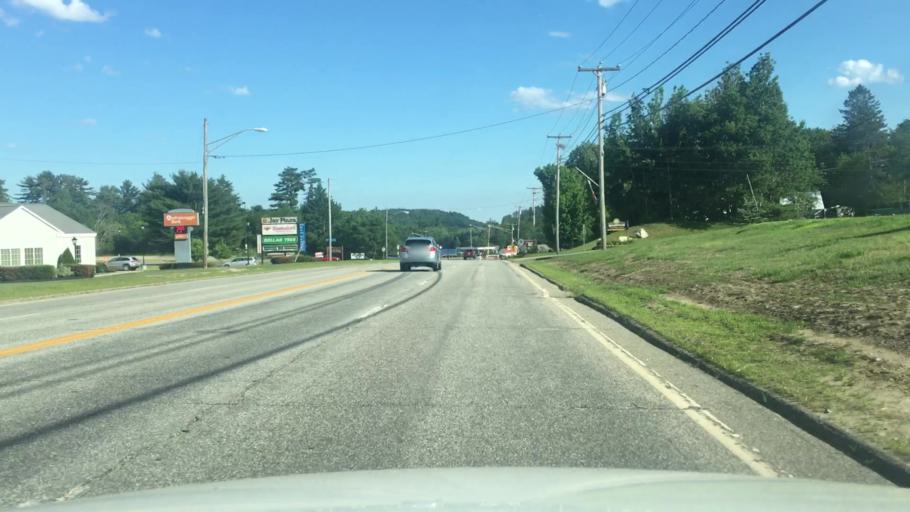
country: US
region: Maine
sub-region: Franklin County
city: Jay
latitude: 44.5062
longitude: -70.2176
